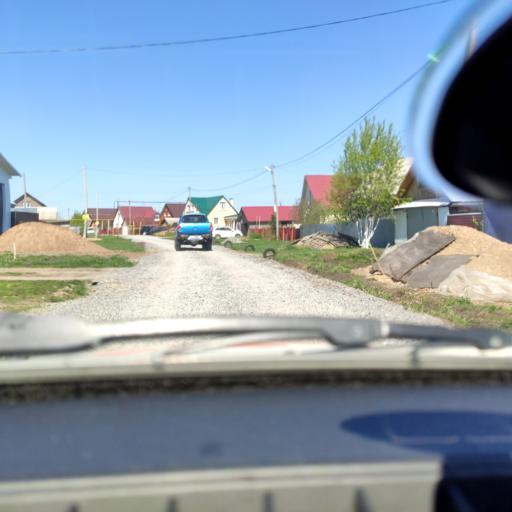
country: RU
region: Bashkortostan
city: Iglino
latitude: 54.7956
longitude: 56.2790
